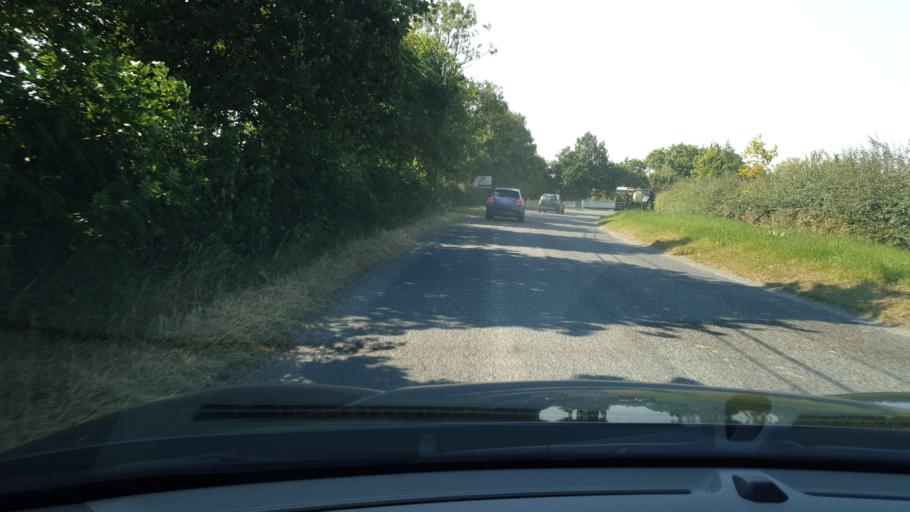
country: IE
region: Leinster
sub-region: An Mhi
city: Trim
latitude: 53.5719
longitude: -6.8262
